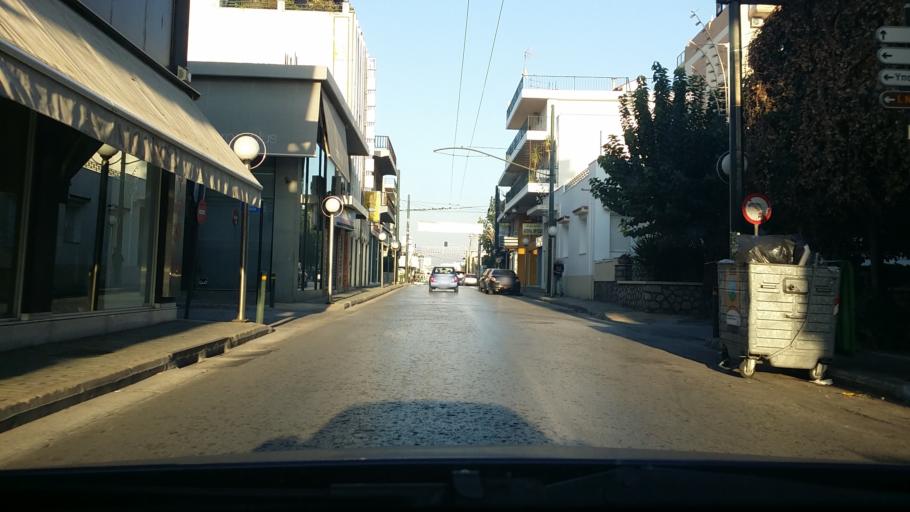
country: GR
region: Attica
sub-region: Nomarchia Athinas
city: Ilion
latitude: 38.0315
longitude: 23.7084
